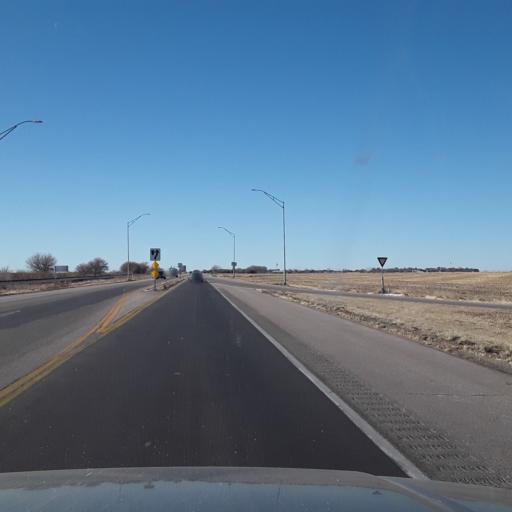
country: US
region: Nebraska
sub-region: Kearney County
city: Minden
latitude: 40.4840
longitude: -99.0852
